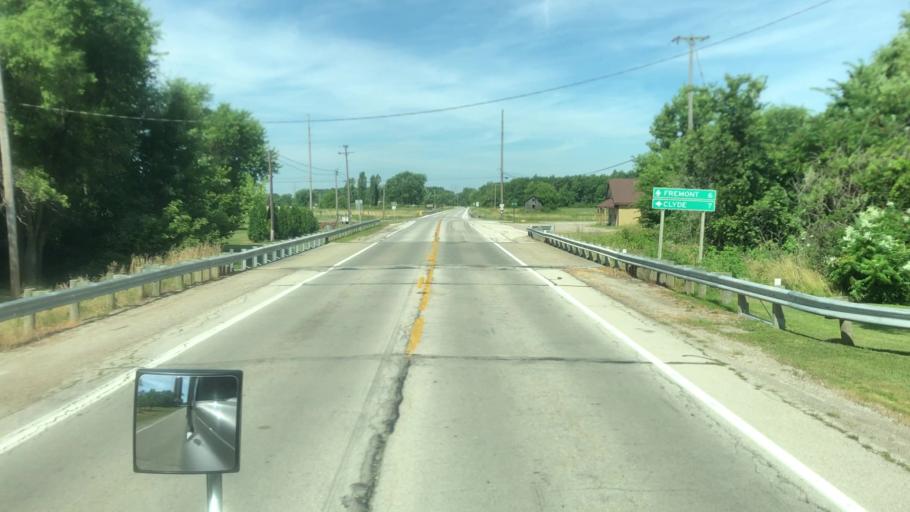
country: US
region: Ohio
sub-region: Sandusky County
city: Clyde
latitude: 41.4086
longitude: -82.9715
